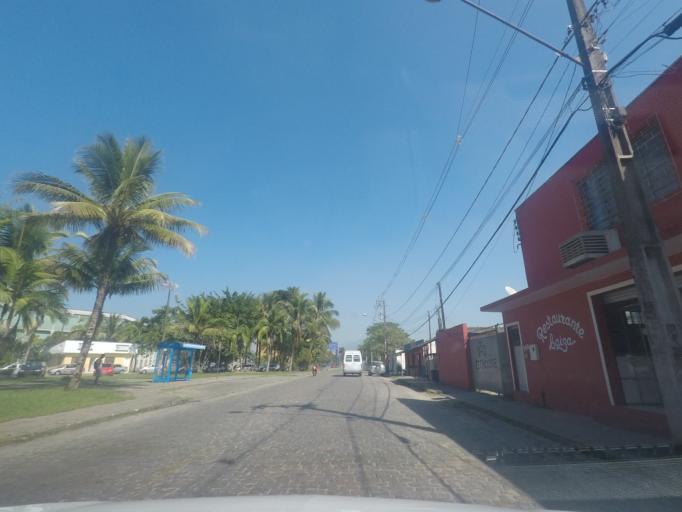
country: BR
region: Parana
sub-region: Paranagua
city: Paranagua
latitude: -25.5229
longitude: -48.5081
